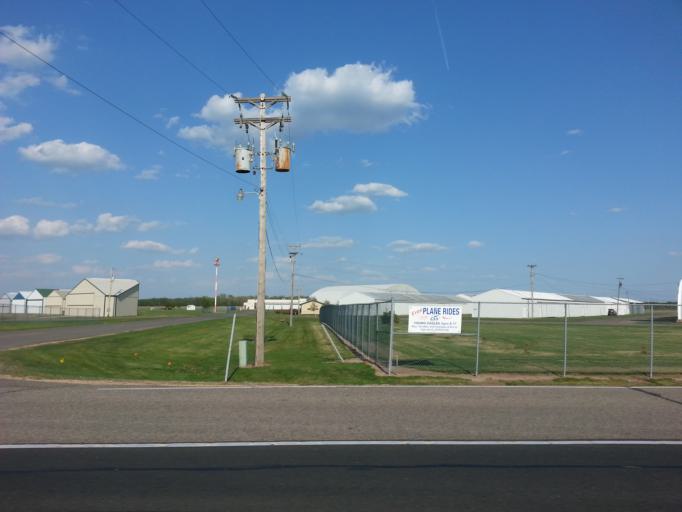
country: US
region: Minnesota
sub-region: Washington County
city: Lake Elmo
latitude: 44.9964
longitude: -92.8628
